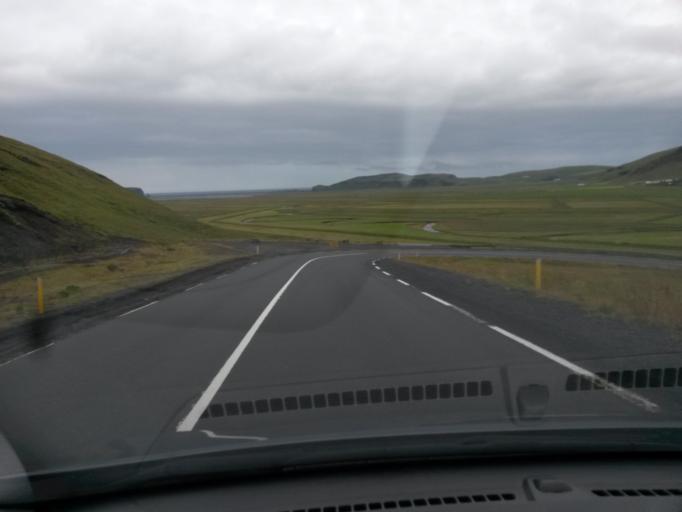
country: IS
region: South
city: Vestmannaeyjar
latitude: 63.4531
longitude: -19.0601
